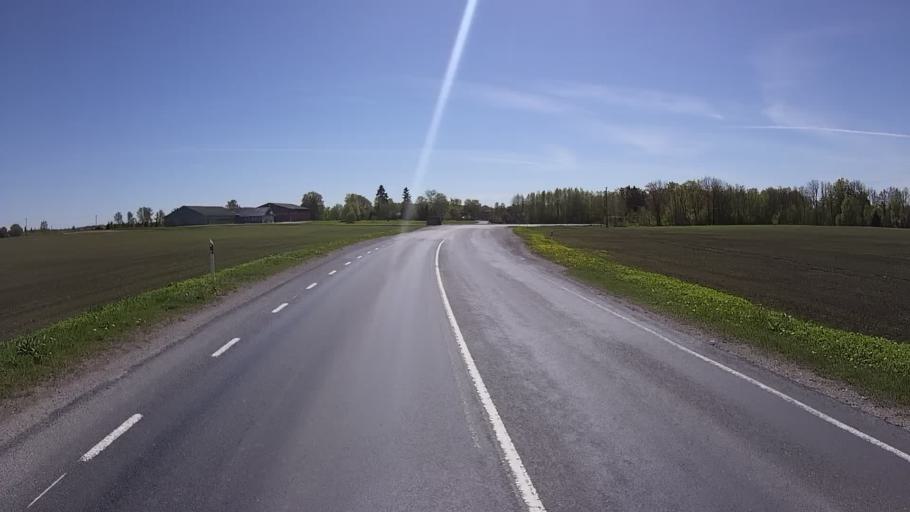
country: EE
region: Harju
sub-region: Anija vald
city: Kehra
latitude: 59.1301
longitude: 25.2045
